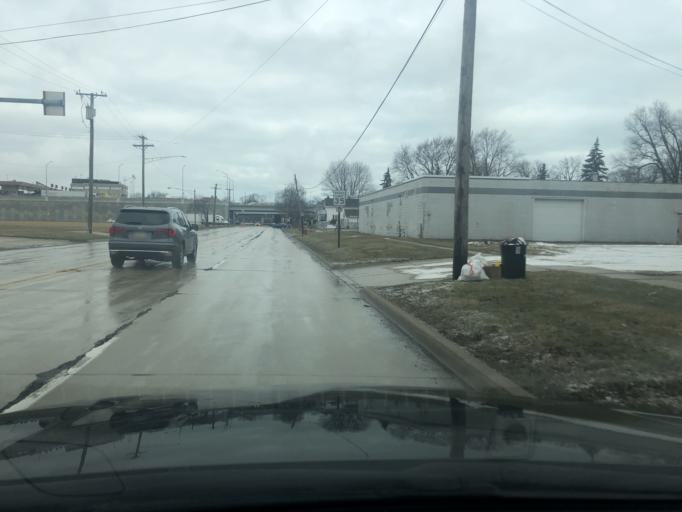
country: US
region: Michigan
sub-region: Saint Clair County
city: Port Huron
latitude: 42.9960
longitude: -82.4343
